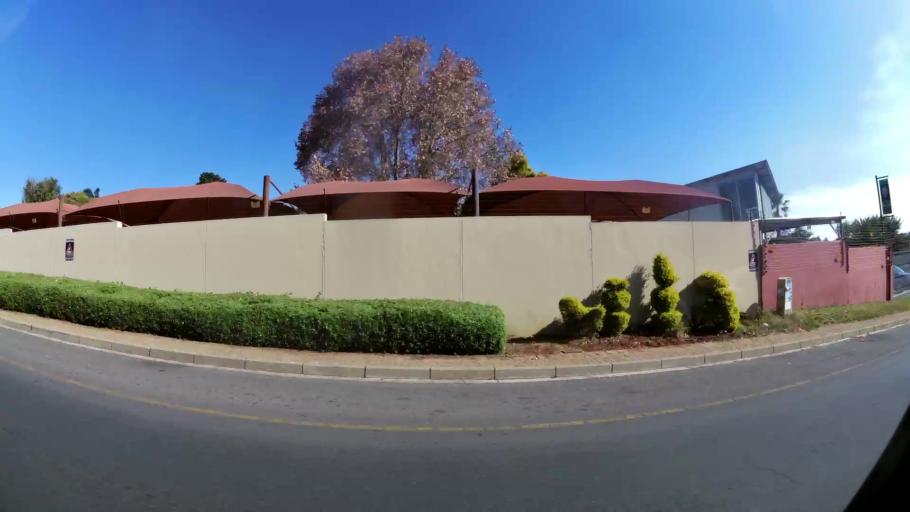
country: ZA
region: Gauteng
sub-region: City of Johannesburg Metropolitan Municipality
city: Roodepoort
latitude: -26.1224
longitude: 27.9615
